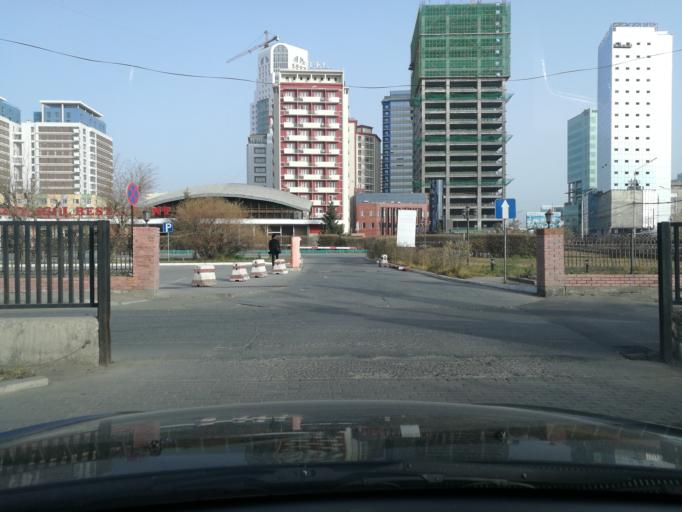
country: MN
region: Ulaanbaatar
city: Ulaanbaatar
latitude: 47.9115
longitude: 106.9143
